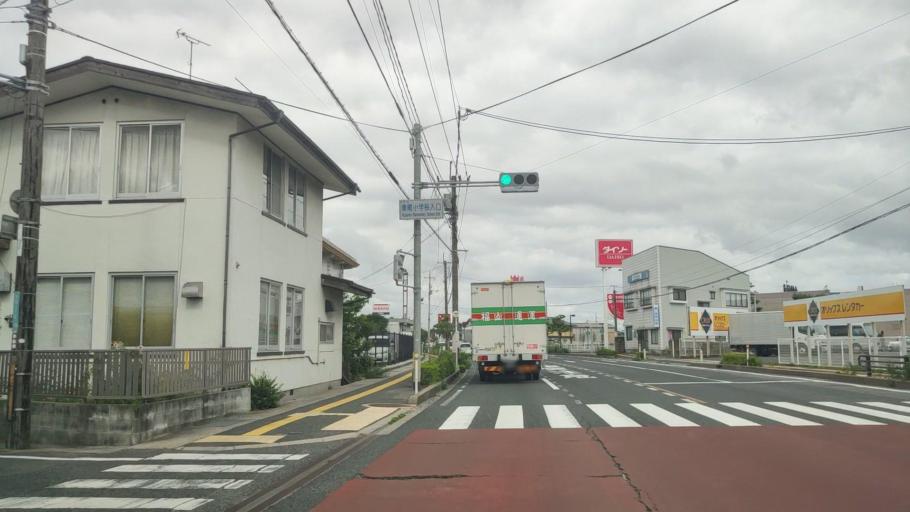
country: JP
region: Tottori
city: Yonago
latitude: 35.4328
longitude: 133.3584
